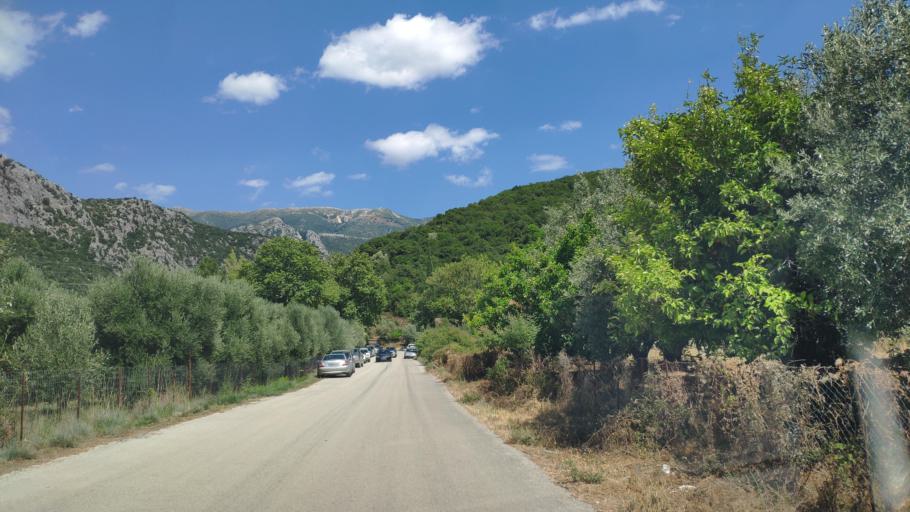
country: GR
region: Epirus
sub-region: Nomos Prevezis
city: Kanalaki
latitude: 39.3244
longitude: 20.6113
